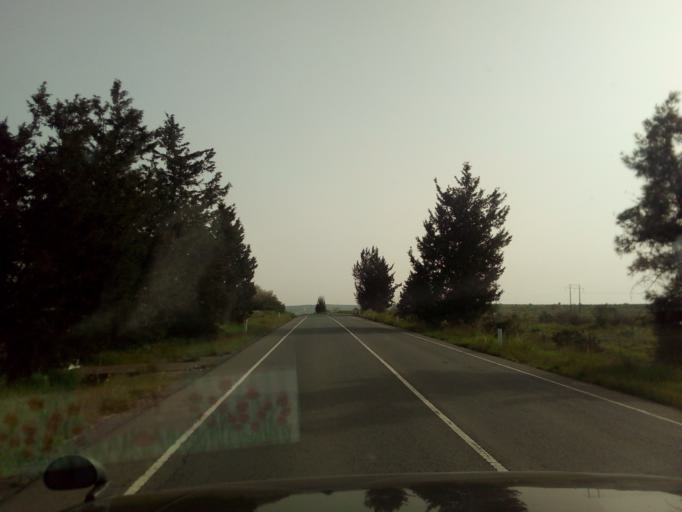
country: CY
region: Lefkosia
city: Lympia
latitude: 35.0087
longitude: 33.4970
